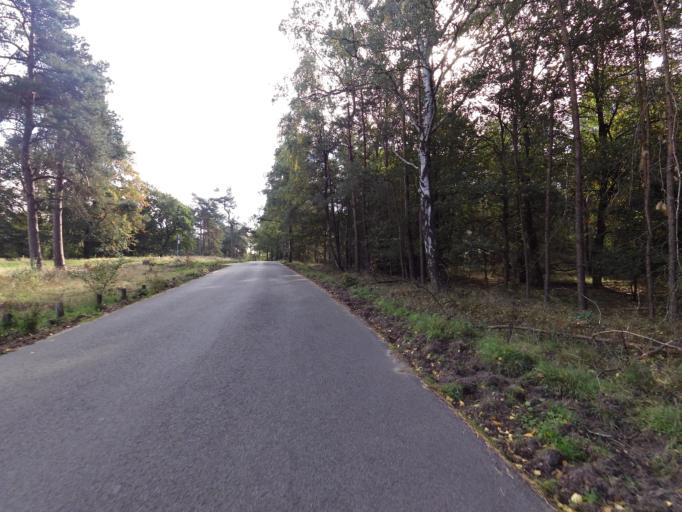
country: NL
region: Gelderland
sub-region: Gemeente Rheden
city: Rheden
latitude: 52.0271
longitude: 6.0026
